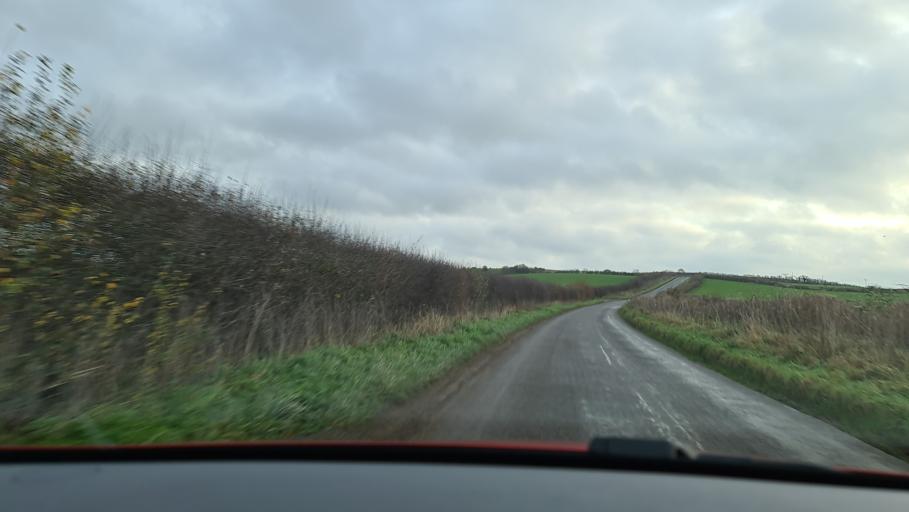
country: GB
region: England
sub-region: Buckinghamshire
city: Long Crendon
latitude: 51.7978
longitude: -0.9779
